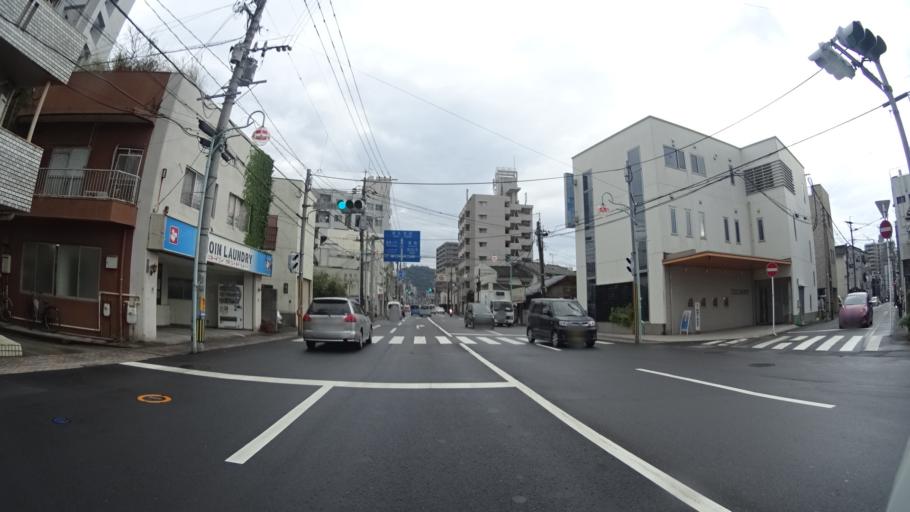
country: JP
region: Kagoshima
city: Kagoshima-shi
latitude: 31.6017
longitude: 130.5607
